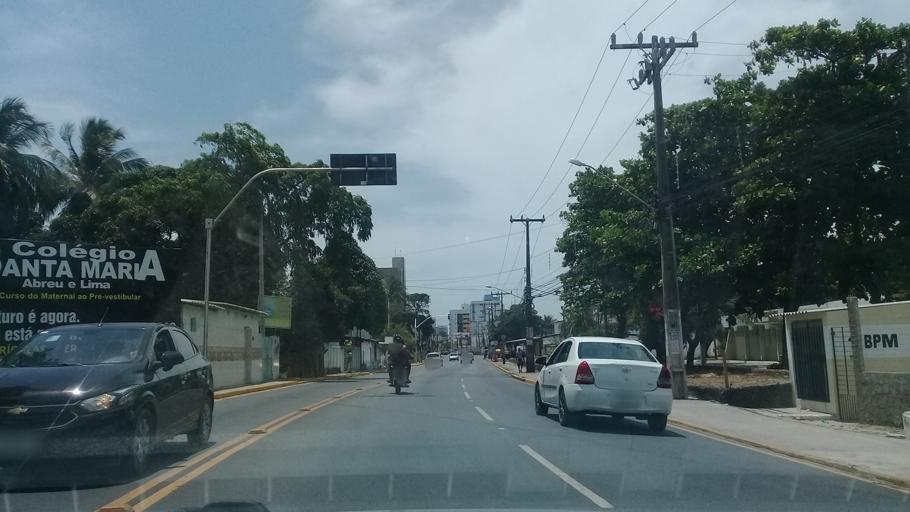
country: BR
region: Pernambuco
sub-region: Paulista
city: Paulista
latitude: -7.9601
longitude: -34.8307
